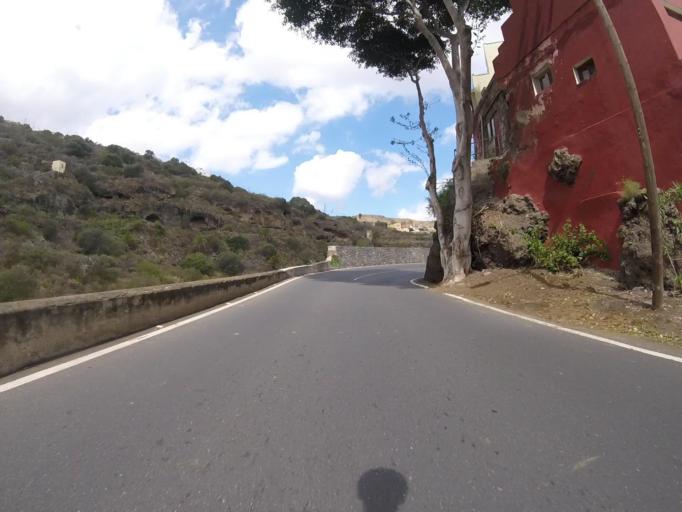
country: ES
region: Canary Islands
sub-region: Provincia de Las Palmas
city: Santa Brigida
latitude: 28.0566
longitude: -15.4759
